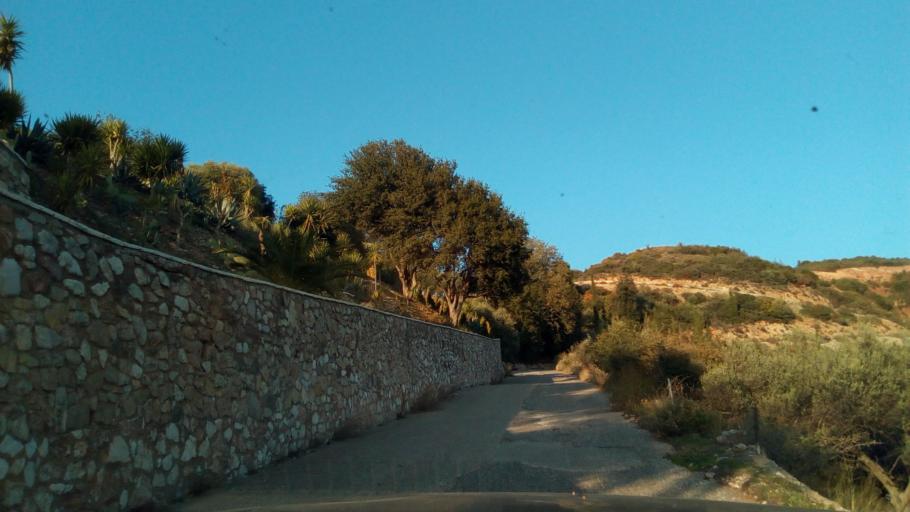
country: GR
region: West Greece
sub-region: Nomos Aitolias kai Akarnanias
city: Nafpaktos
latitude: 38.4232
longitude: 21.8449
